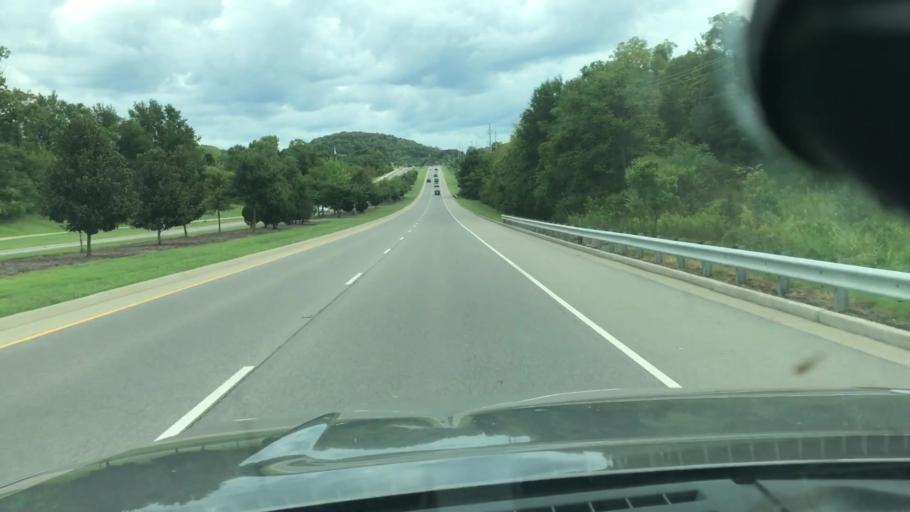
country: US
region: Tennessee
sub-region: Williamson County
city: Franklin
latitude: 35.9198
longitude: -86.8439
